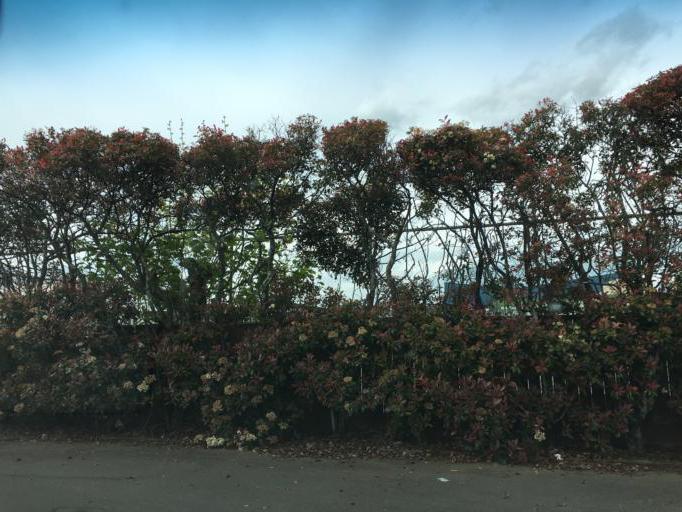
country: NZ
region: Manawatu-Wanganui
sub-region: Palmerston North City
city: Palmerston North
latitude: -40.3493
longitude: 175.6063
